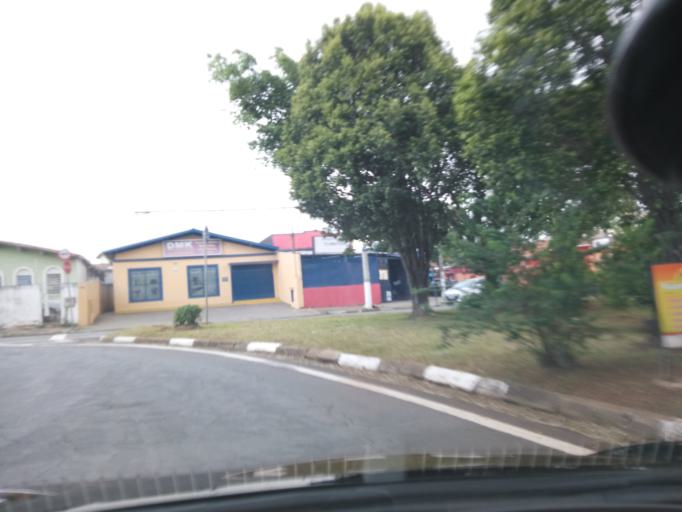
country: BR
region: Sao Paulo
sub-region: Campinas
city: Campinas
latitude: -22.8794
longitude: -47.0367
